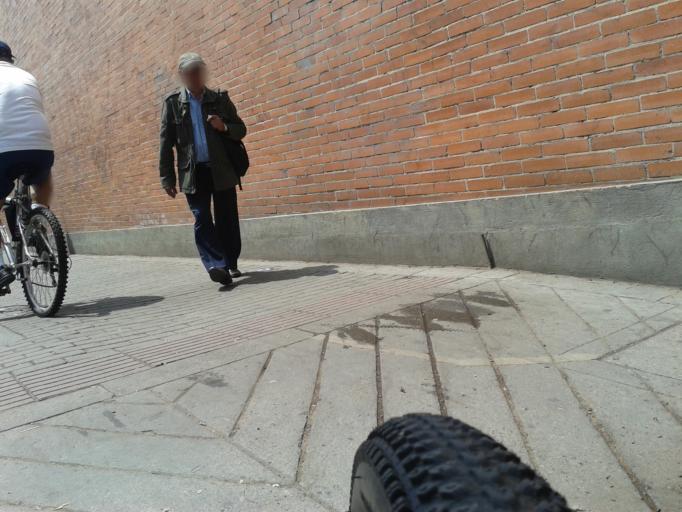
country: CO
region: Bogota D.C.
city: Barrio San Luis
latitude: 4.7219
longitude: -74.0750
